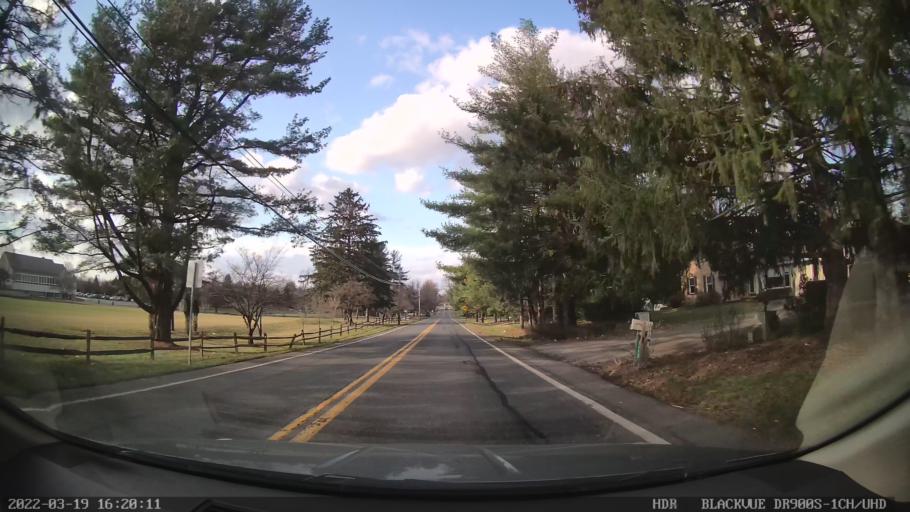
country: US
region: Pennsylvania
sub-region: Lehigh County
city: Dorneyville
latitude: 40.5779
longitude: -75.5023
